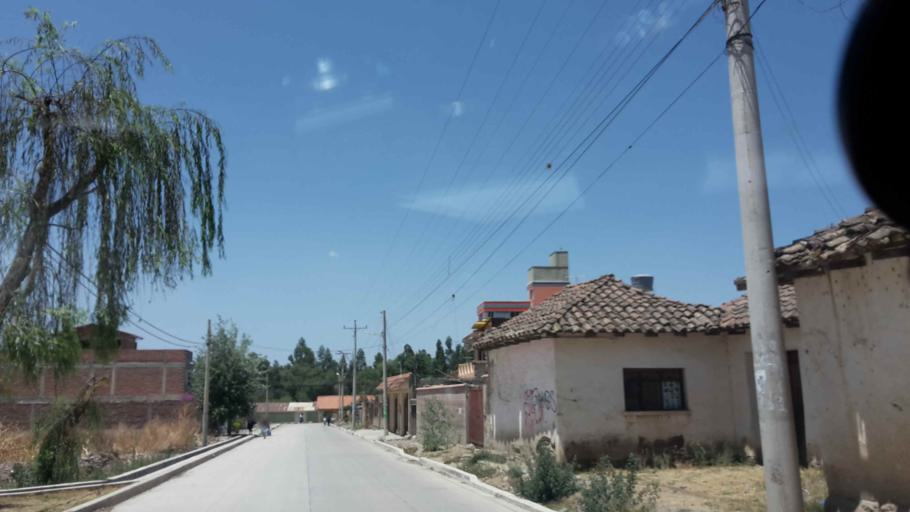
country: BO
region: Cochabamba
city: Cochabamba
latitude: -17.3548
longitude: -66.2074
